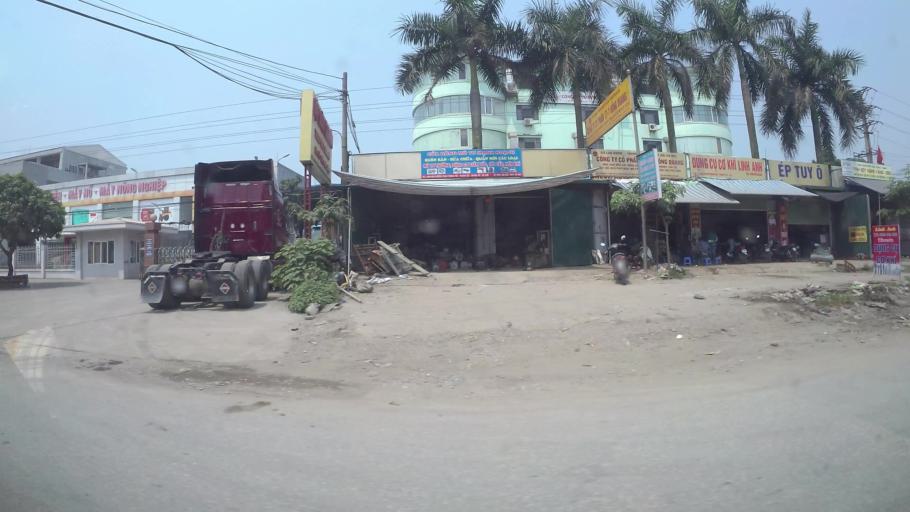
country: VN
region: Ha Noi
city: Van Dien
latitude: 20.9520
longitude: 105.8178
